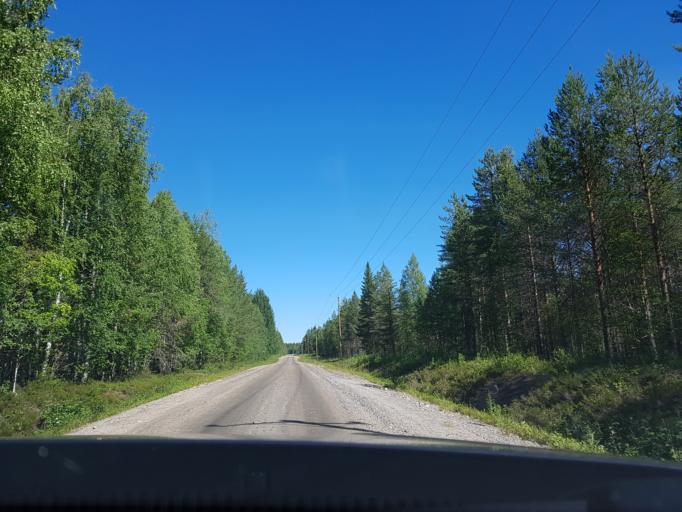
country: FI
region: Kainuu
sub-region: Kehys-Kainuu
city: Kuhmo
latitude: 64.1865
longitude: 29.5974
